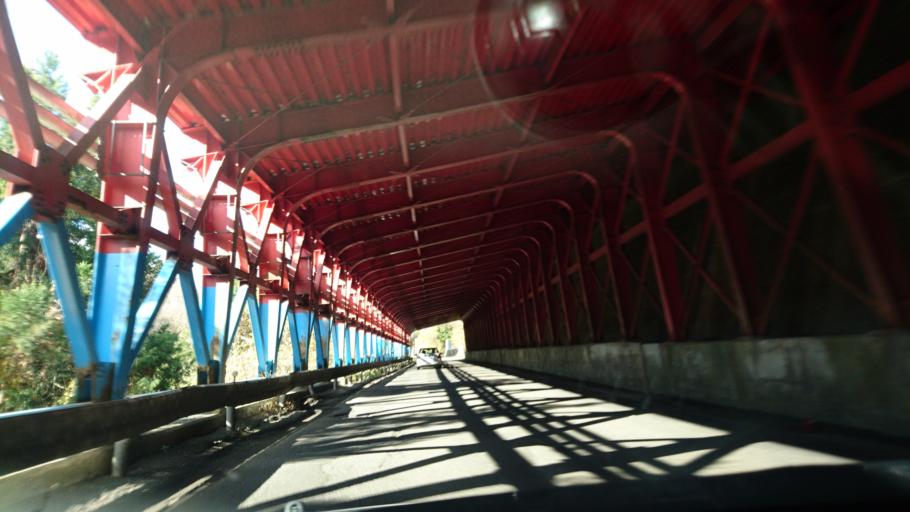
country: JP
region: Akita
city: Yuzawa
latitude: 39.2724
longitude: 140.3418
